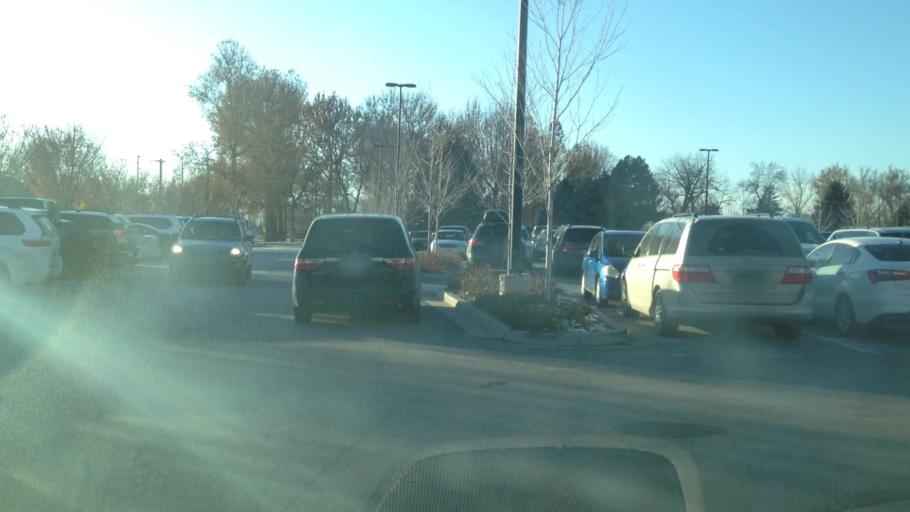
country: US
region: Utah
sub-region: Utah County
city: Provo
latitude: 40.2407
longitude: -111.6641
